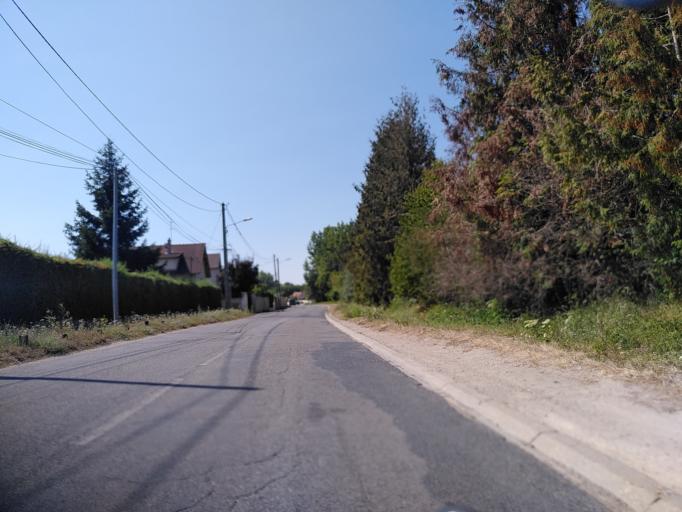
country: FR
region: Ile-de-France
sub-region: Departement de l'Essonne
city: Saint-Germain-les-Arpajon
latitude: 48.6017
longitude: 2.2669
